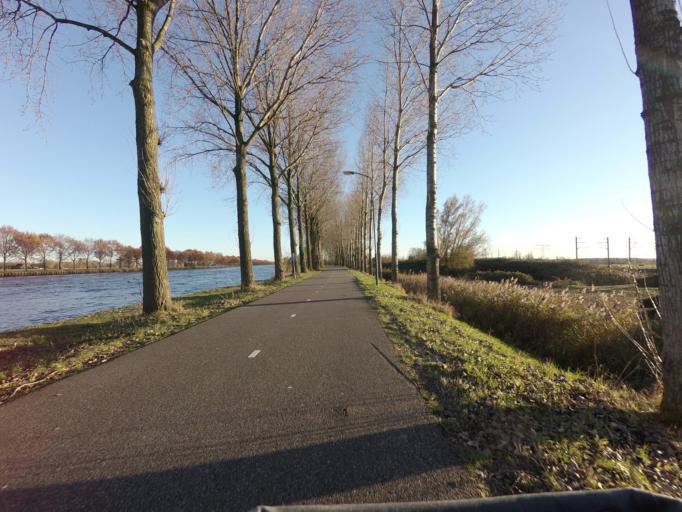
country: NL
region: Utrecht
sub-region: Stichtse Vecht
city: Breukelen
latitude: 52.1559
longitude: 4.9996
